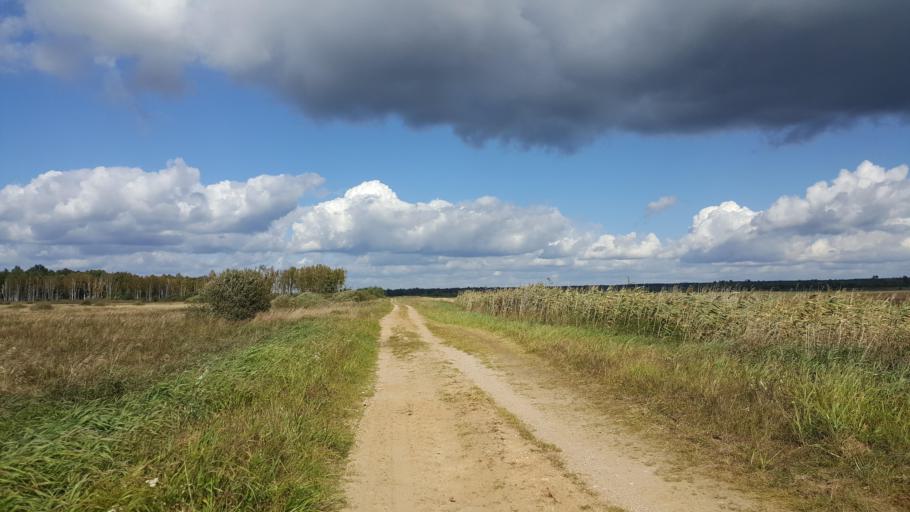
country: BY
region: Brest
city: Kamyanyets
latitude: 52.4494
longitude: 23.9345
